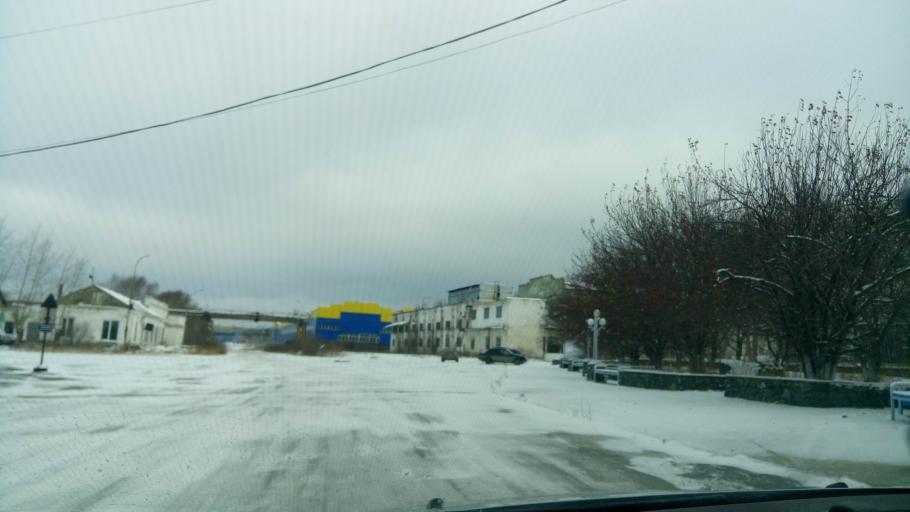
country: RU
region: Sverdlovsk
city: Polevskoy
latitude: 56.4677
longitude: 60.1785
